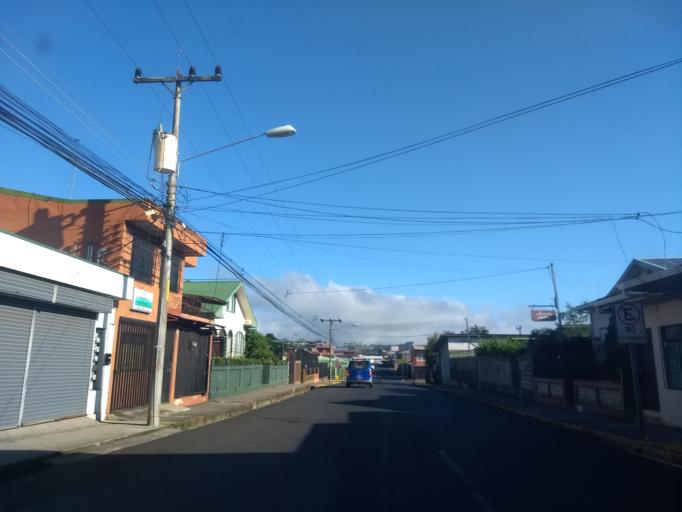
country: CR
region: Alajuela
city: San Ramon
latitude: 10.0894
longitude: -84.4686
